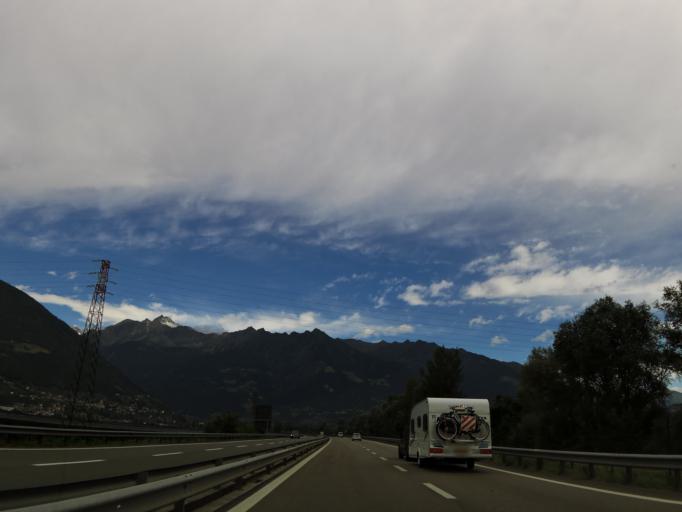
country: IT
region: Trentino-Alto Adige
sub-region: Bolzano
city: Sinigo
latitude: 46.6358
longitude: 11.1711
